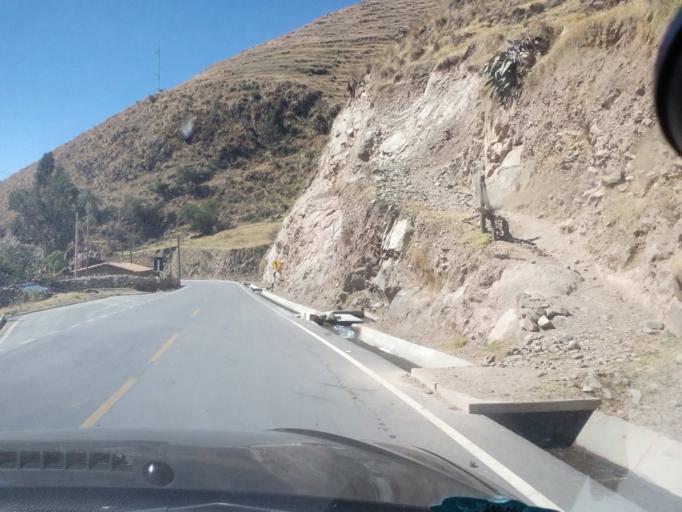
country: PE
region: Ayacucho
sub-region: Provincia de Huamanga
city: Ocros
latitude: -13.3922
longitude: -73.9237
